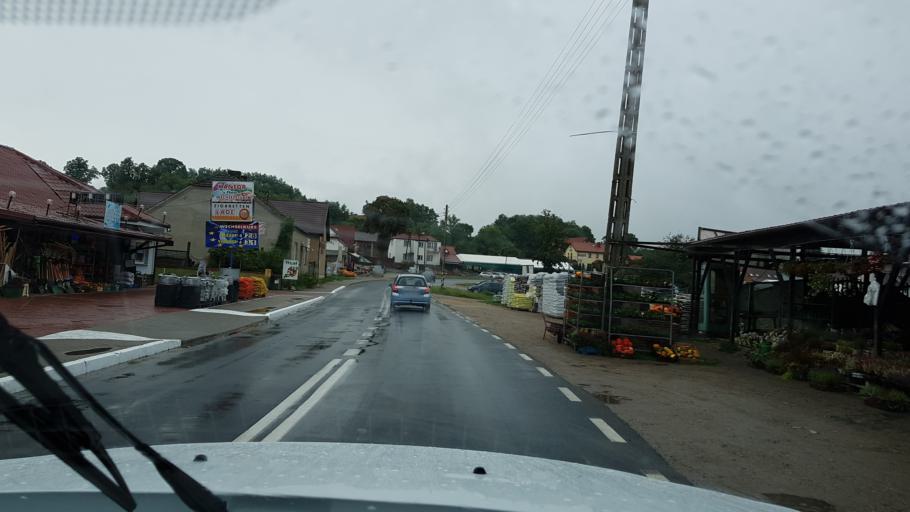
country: DE
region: Brandenburg
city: Schwedt (Oder)
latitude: 53.0326
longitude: 14.3199
